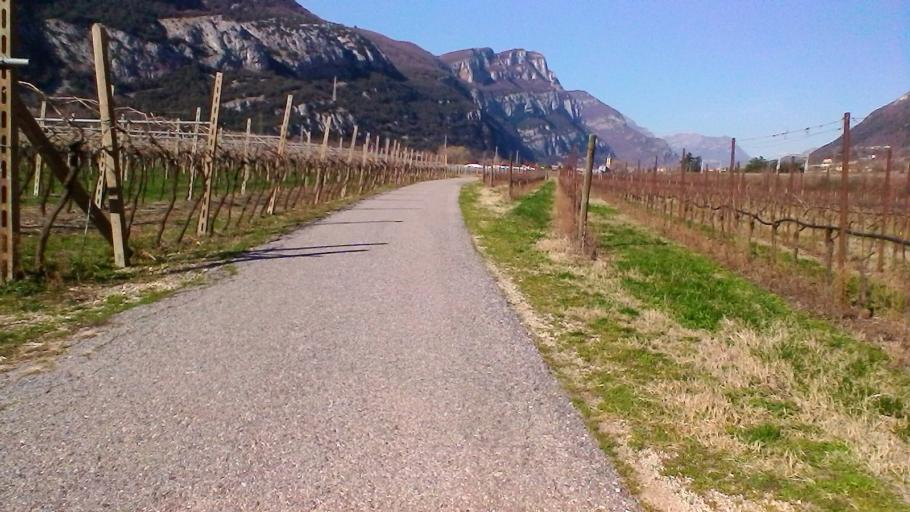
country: IT
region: Veneto
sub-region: Provincia di Verona
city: Dolce
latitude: 45.5923
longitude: 10.8462
